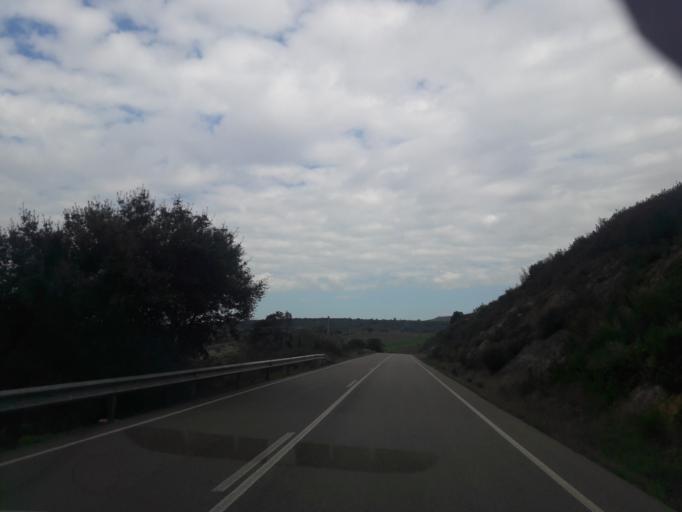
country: ES
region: Castille and Leon
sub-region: Provincia de Salamanca
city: Serradilla del Arroyo
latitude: 40.5173
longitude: -6.3643
